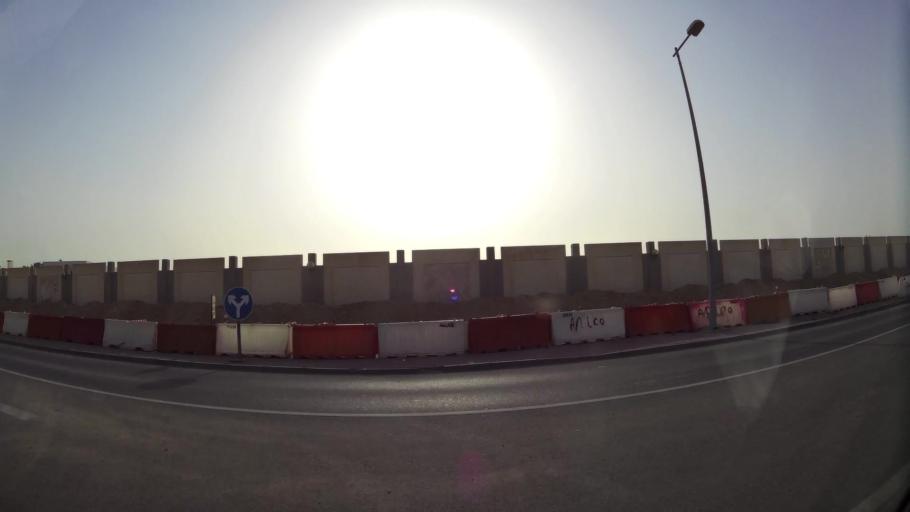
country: QA
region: Baladiyat ar Rayyan
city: Ar Rayyan
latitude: 25.2436
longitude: 51.4381
